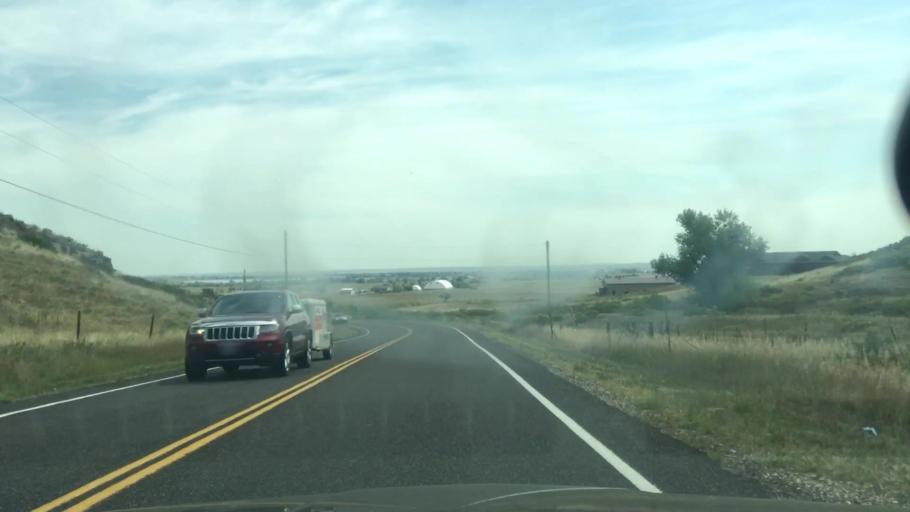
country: US
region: Colorado
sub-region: Larimer County
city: Campion
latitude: 40.3376
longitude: -105.1793
